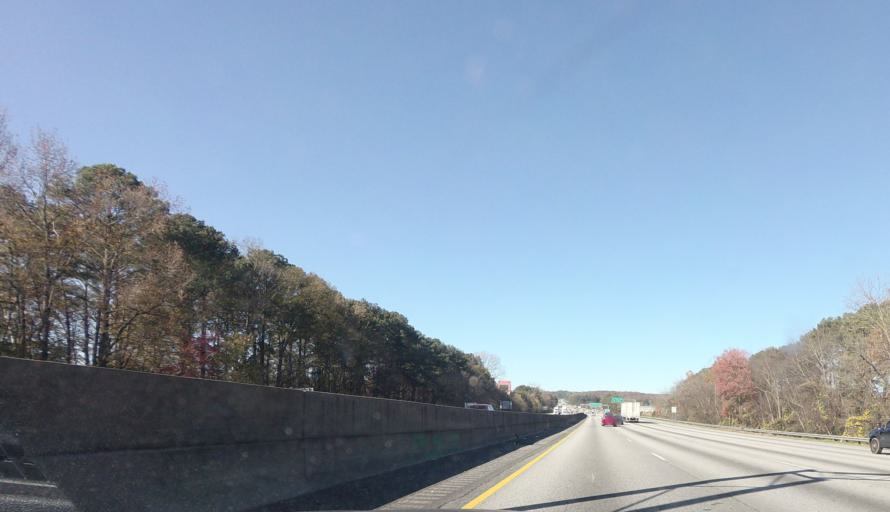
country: US
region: Georgia
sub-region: Cobb County
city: Mableton
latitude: 33.7705
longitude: -84.5416
